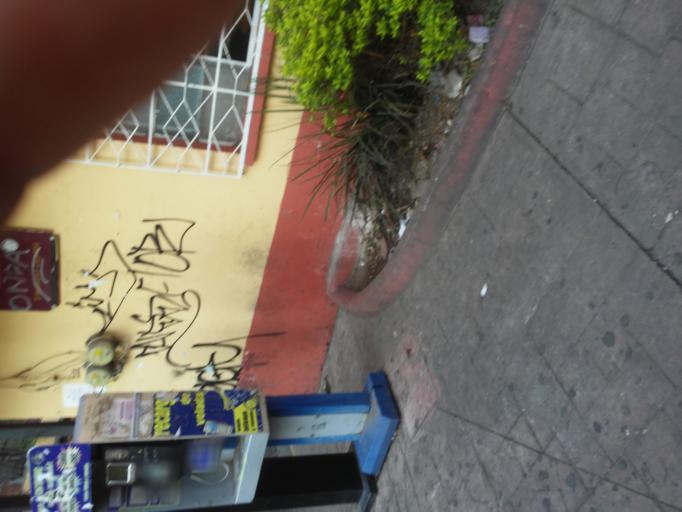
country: MX
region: Guerrero
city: Chilpancingo de los Bravos
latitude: 17.5529
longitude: -99.5023
